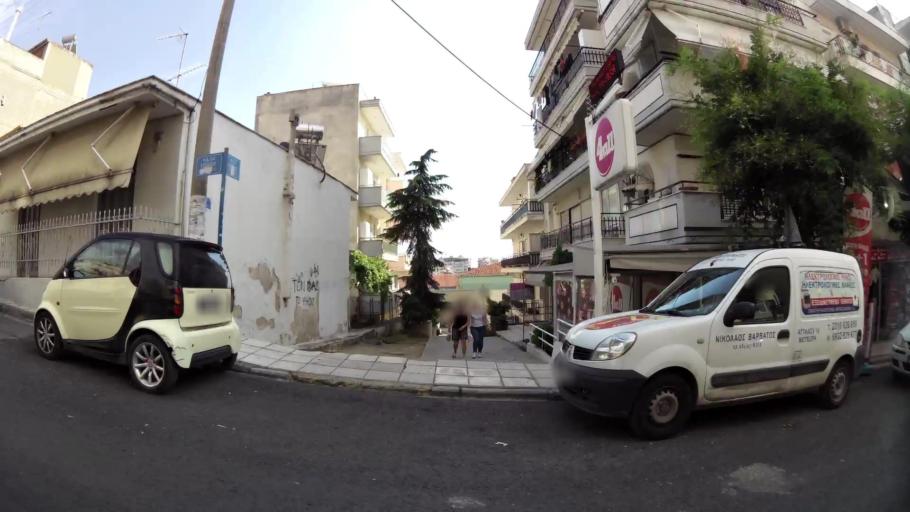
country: GR
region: Central Macedonia
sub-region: Nomos Thessalonikis
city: Sykies
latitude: 40.6569
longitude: 22.9583
